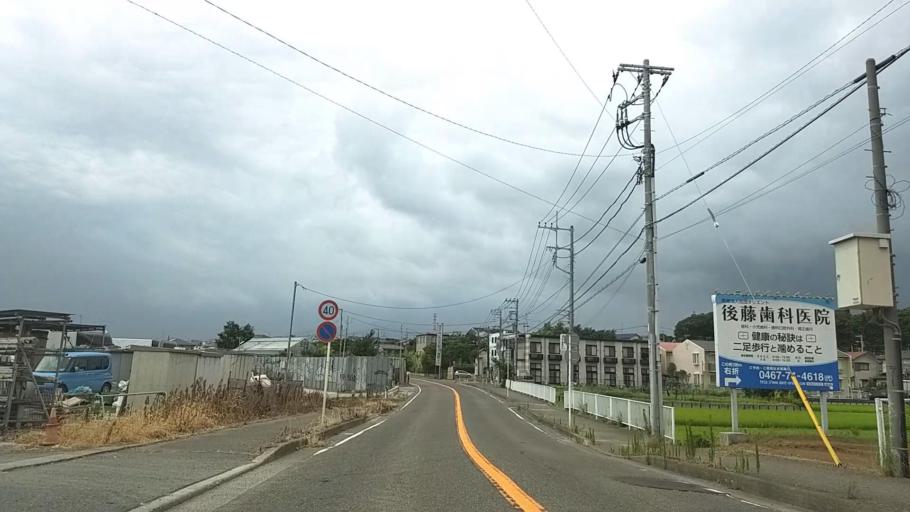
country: JP
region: Kanagawa
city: Chigasaki
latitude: 35.3684
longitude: 139.4008
